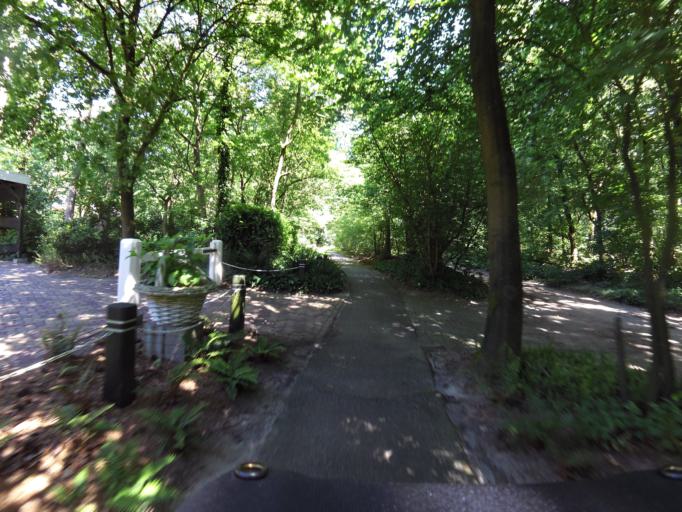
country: NL
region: Overijssel
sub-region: Gemeente Twenterand
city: Den Ham
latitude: 52.4919
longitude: 6.4277
